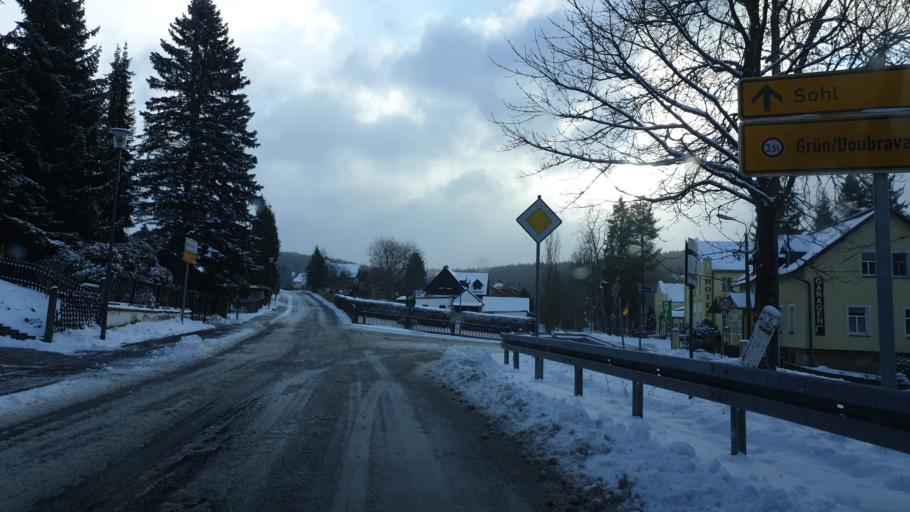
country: DE
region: Saxony
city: Bad Elster
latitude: 50.2756
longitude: 12.2464
